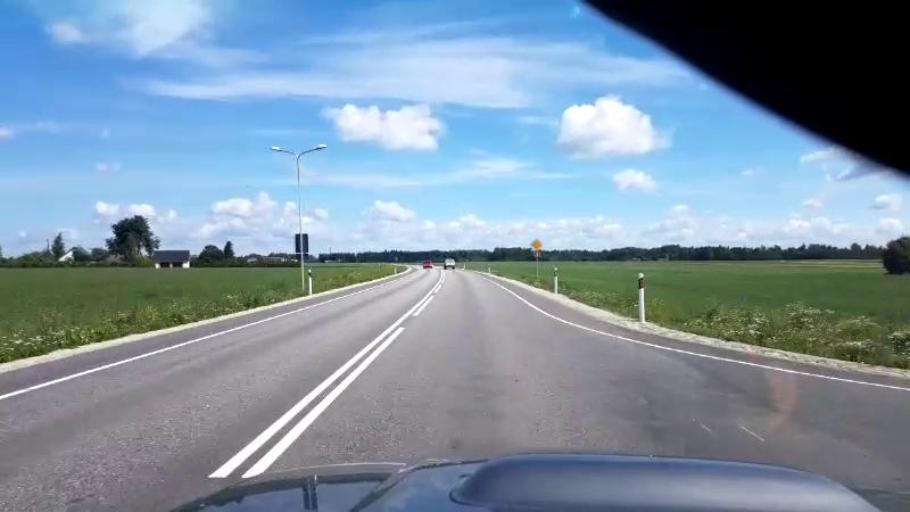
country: EE
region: Jaervamaa
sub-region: Jaerva-Jaani vald
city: Jarva-Jaani
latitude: 59.1156
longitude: 25.7329
